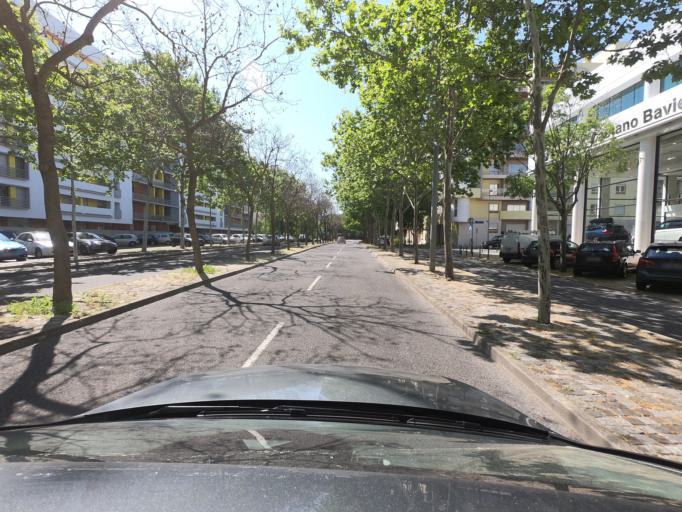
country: PT
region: Lisbon
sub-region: Loures
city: Moscavide
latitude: 38.7829
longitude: -9.0979
